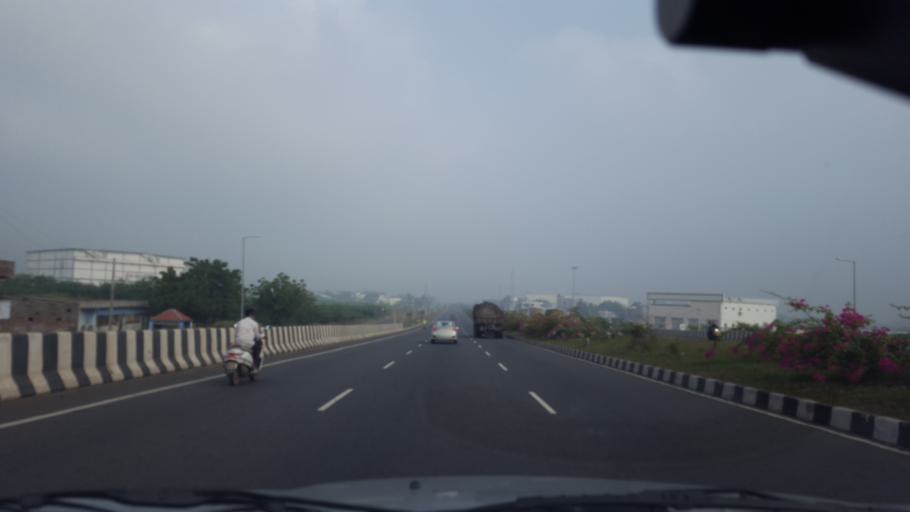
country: IN
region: Andhra Pradesh
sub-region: Prakasam
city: Ongole
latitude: 15.5548
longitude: 80.0547
